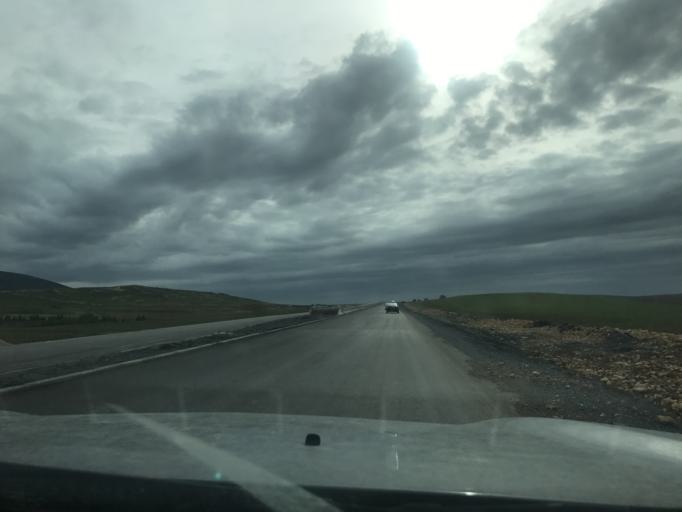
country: TN
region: Silyanah
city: Siliana
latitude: 36.1092
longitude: 9.5885
